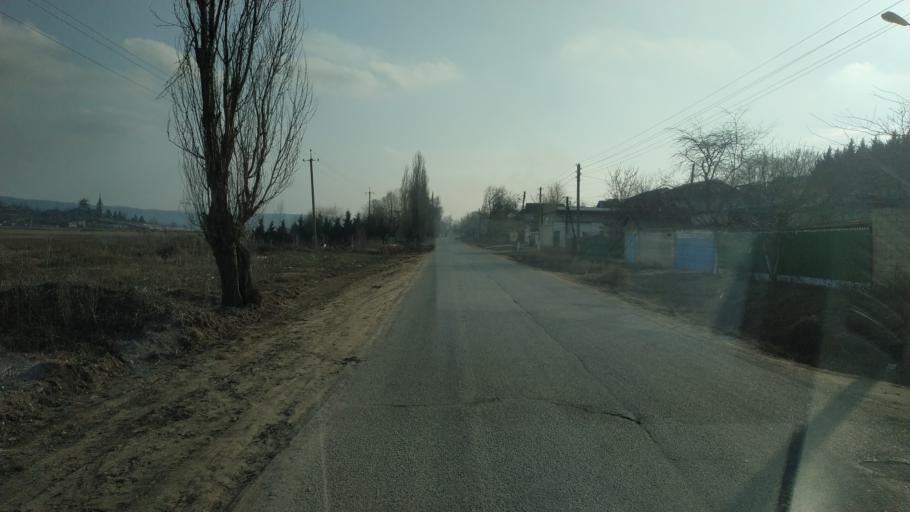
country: MD
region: Hincesti
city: Dancu
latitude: 46.7814
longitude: 28.3489
